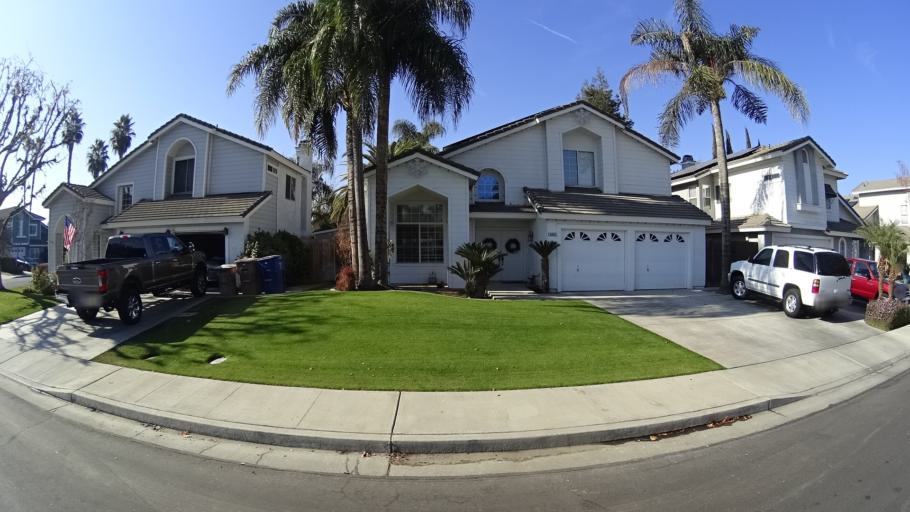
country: US
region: California
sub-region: Kern County
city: Greenacres
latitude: 35.3200
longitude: -119.1212
